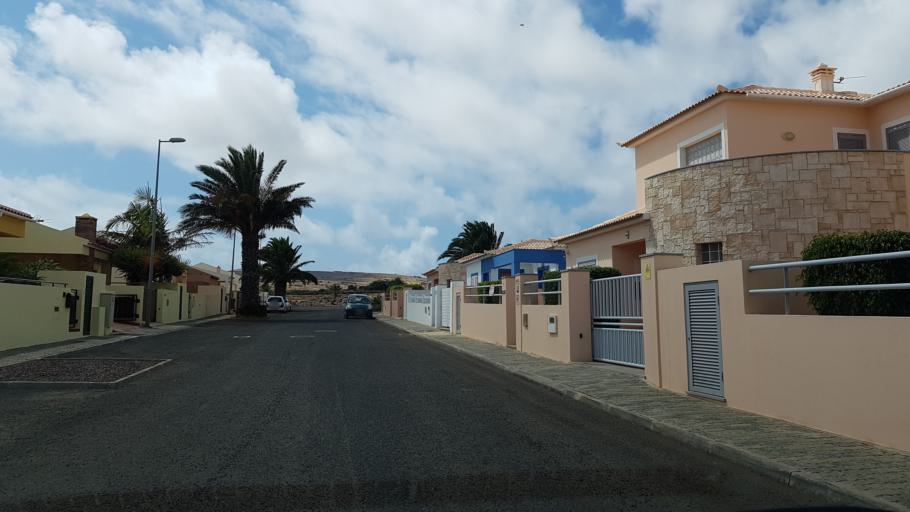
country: PT
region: Madeira
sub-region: Porto Santo
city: Vila de Porto Santo
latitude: 33.0617
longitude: -16.3414
